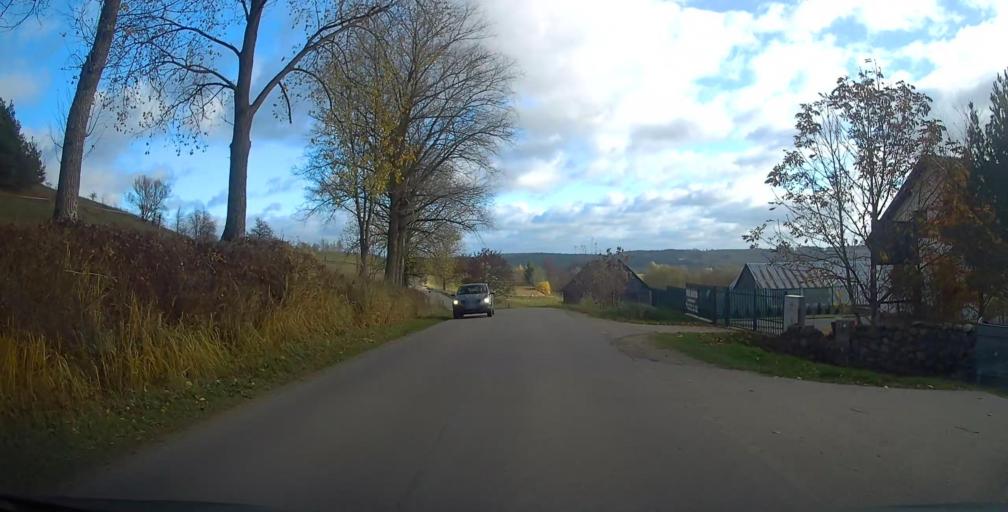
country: PL
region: Podlasie
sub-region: Suwalki
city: Suwalki
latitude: 54.2843
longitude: 22.8943
